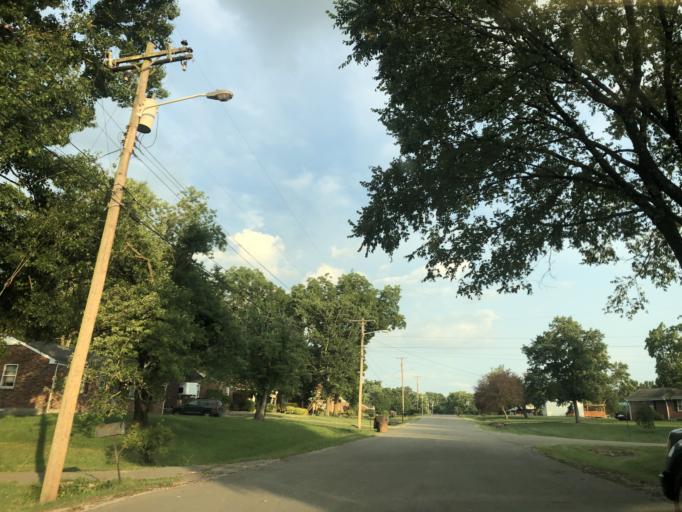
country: US
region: Tennessee
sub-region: Davidson County
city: Nashville
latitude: 36.1654
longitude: -86.7081
